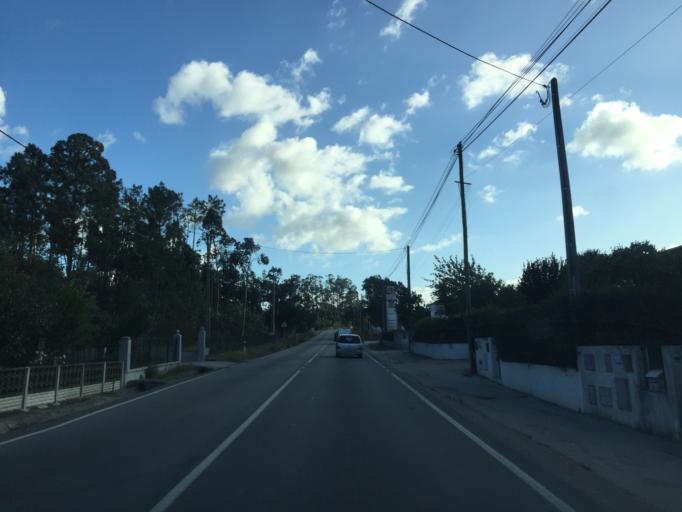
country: PT
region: Leiria
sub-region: Leiria
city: Souto da Carpalhosa
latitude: 39.8579
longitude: -8.8352
